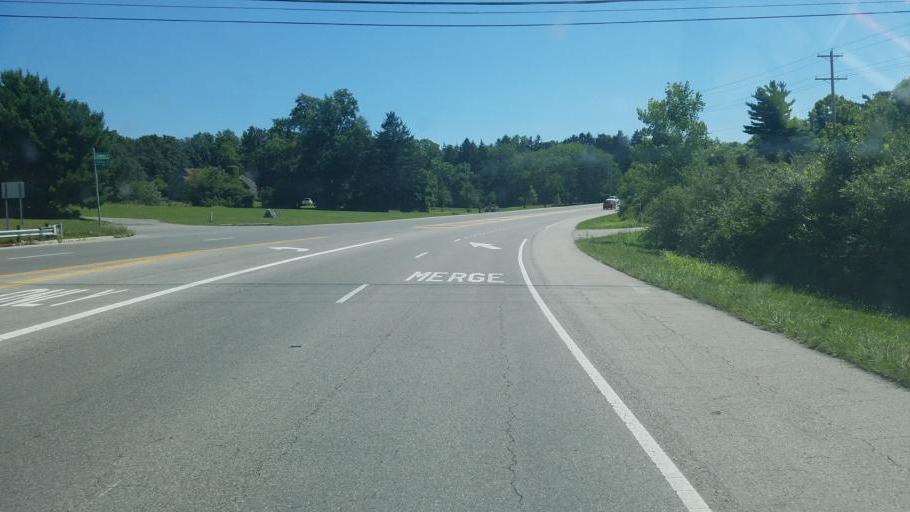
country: US
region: Ohio
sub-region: Franklin County
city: Huber Ridge
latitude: 40.0787
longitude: -82.8961
